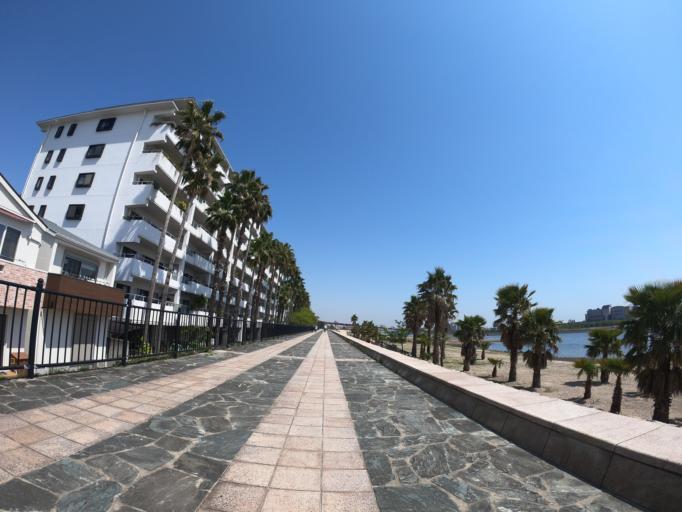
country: JP
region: Hyogo
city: Nishinomiya-hama
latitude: 34.7254
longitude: 135.3268
